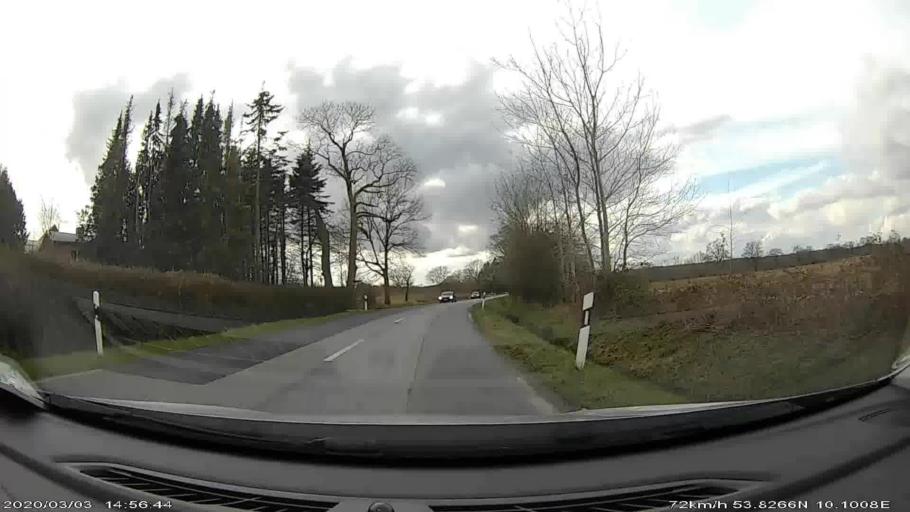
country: DE
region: Schleswig-Holstein
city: Sievershutten
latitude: 53.8268
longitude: 10.1011
